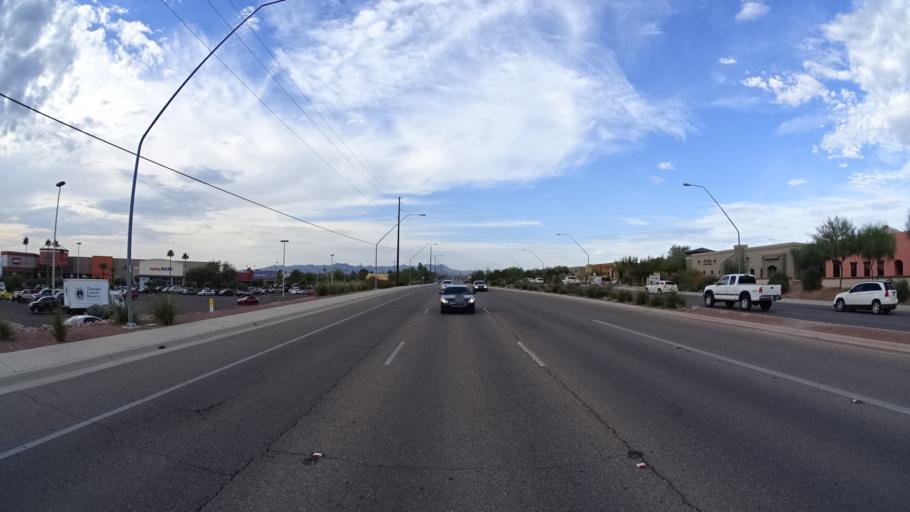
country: US
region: Arizona
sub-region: Pima County
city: Casas Adobes
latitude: 32.3412
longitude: -111.0128
